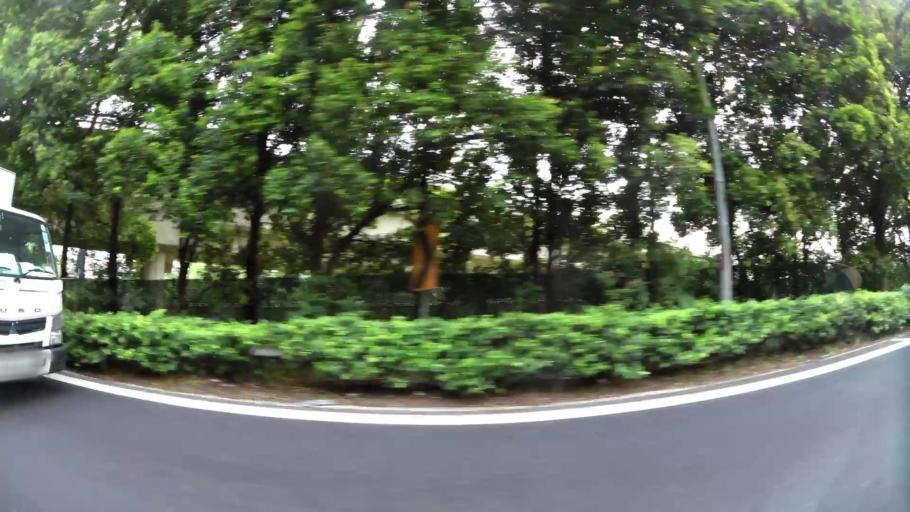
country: MY
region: Johor
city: Johor Bahru
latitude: 1.4194
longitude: 103.7700
